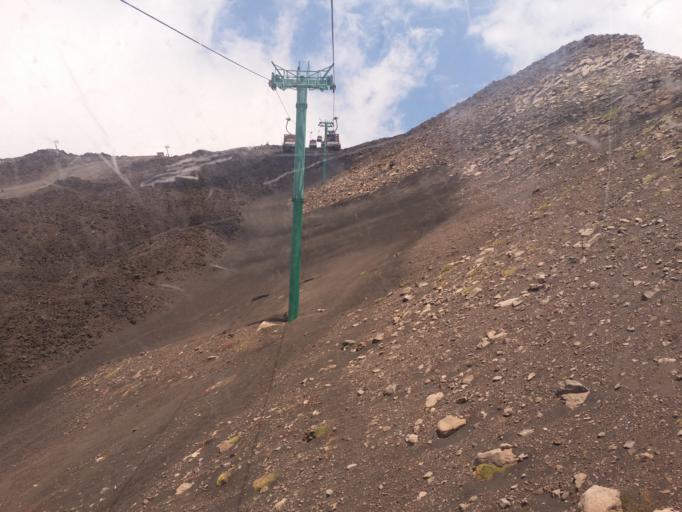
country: IT
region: Sicily
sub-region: Catania
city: Ragalna
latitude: 37.7140
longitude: 14.9998
